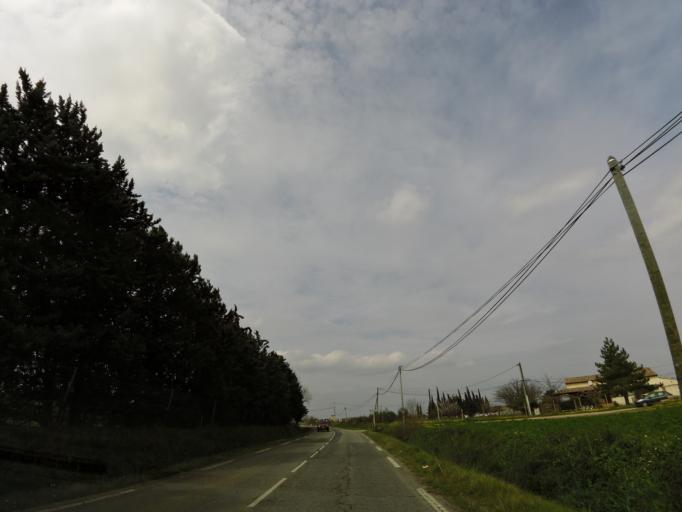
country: FR
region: Languedoc-Roussillon
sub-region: Departement du Gard
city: Aimargues
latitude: 43.6863
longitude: 4.2007
